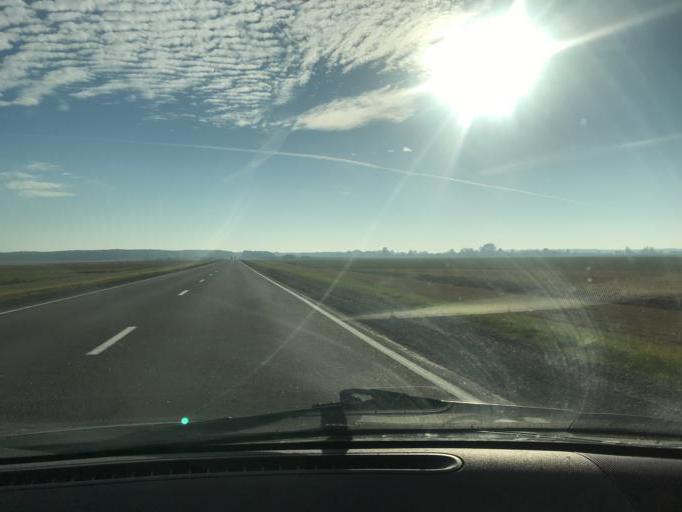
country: BY
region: Brest
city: Drahichyn
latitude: 52.1912
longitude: 25.2638
